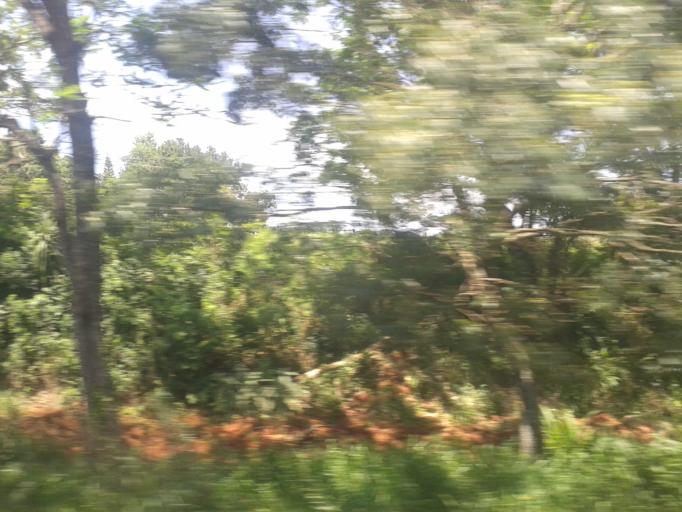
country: AR
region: Misiones
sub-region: Departamento de Leandro N. Alem
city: Leandro N. Alem
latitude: -27.6033
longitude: -55.3408
